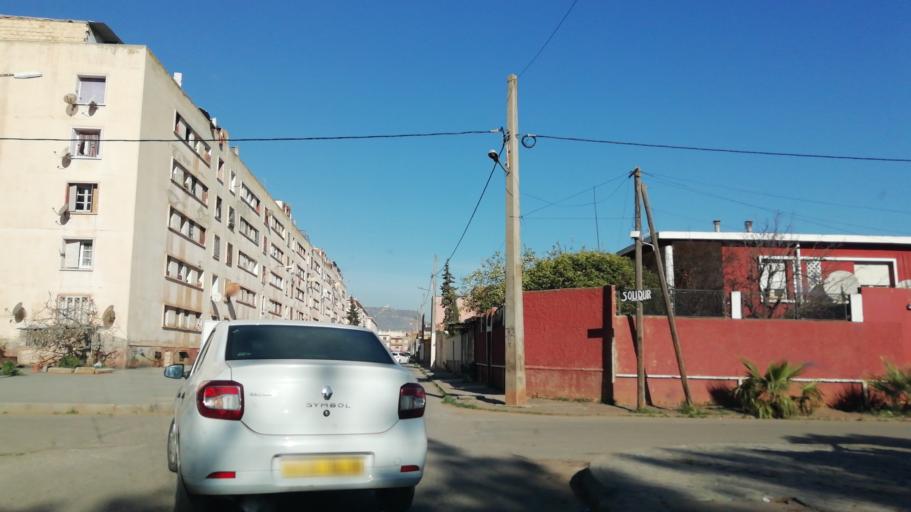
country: DZ
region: Oran
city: Oran
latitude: 35.6712
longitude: -0.6479
